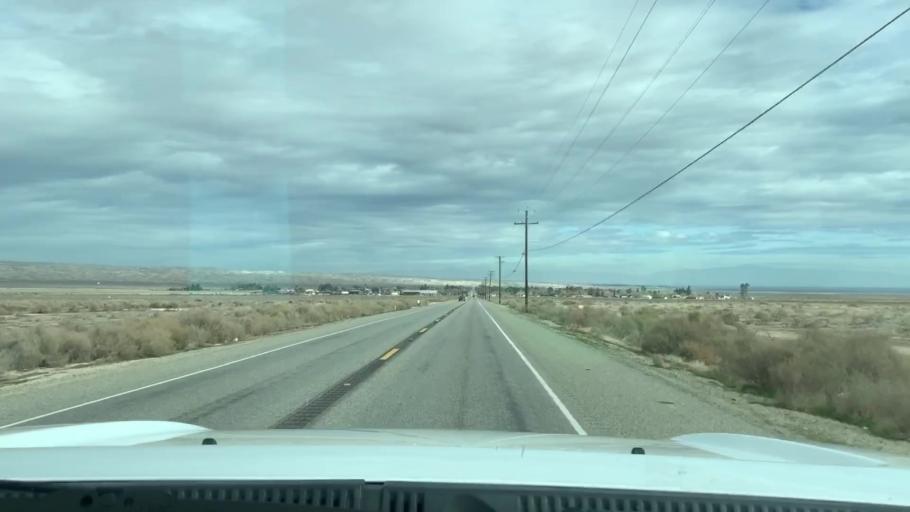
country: US
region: California
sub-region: Kern County
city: Ford City
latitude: 35.1980
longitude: -119.4224
